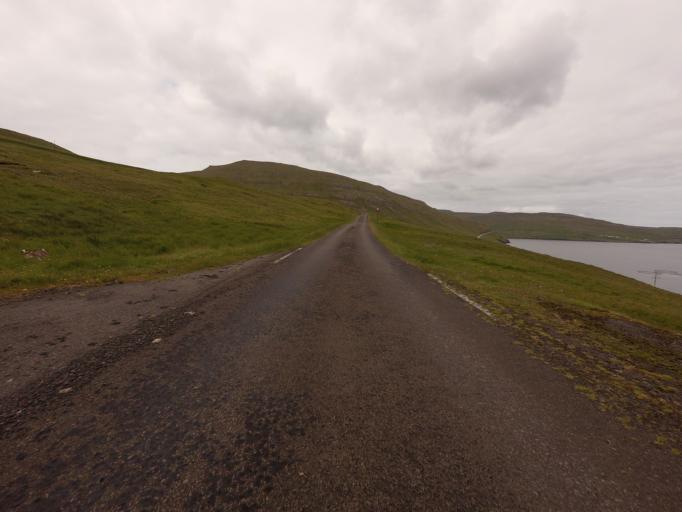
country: FO
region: Suduroy
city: Vagur
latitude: 61.4408
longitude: -6.7749
